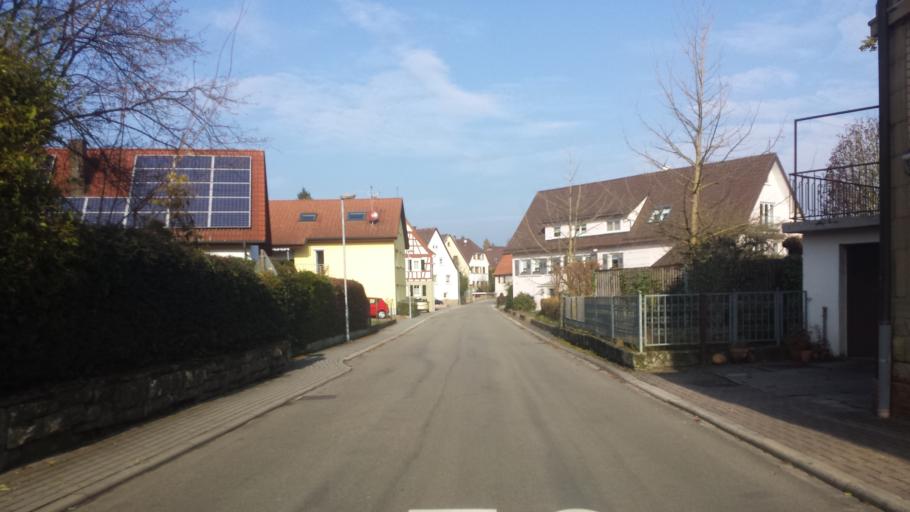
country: DE
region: Baden-Wuerttemberg
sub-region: Karlsruhe Region
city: Neckarbischofsheim
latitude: 49.3218
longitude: 8.9735
